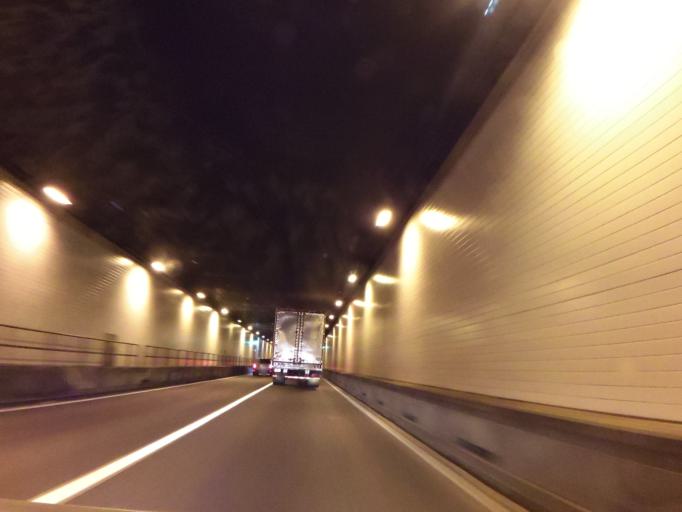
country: US
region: Virginia
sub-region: Bland County
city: Bland
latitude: 37.0376
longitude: -81.1290
